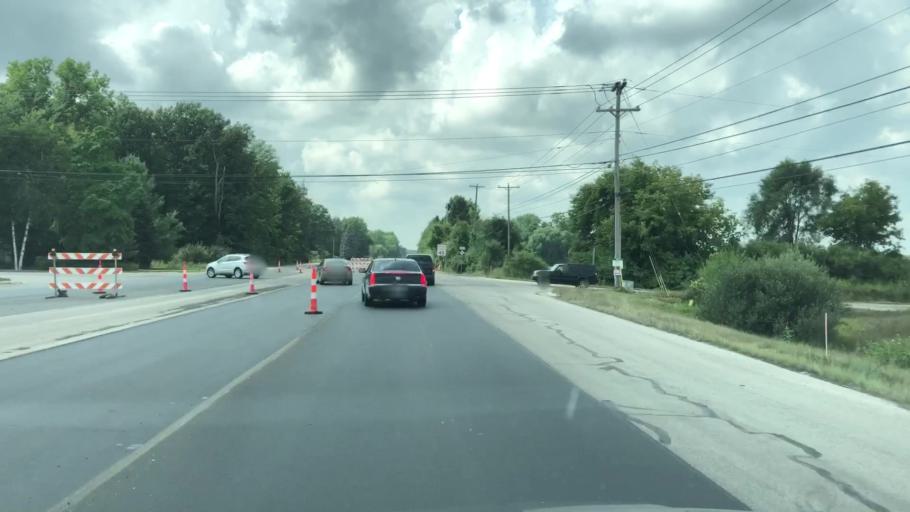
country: US
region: Michigan
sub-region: Isabella County
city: Mount Pleasant
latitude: 43.6120
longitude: -84.6873
